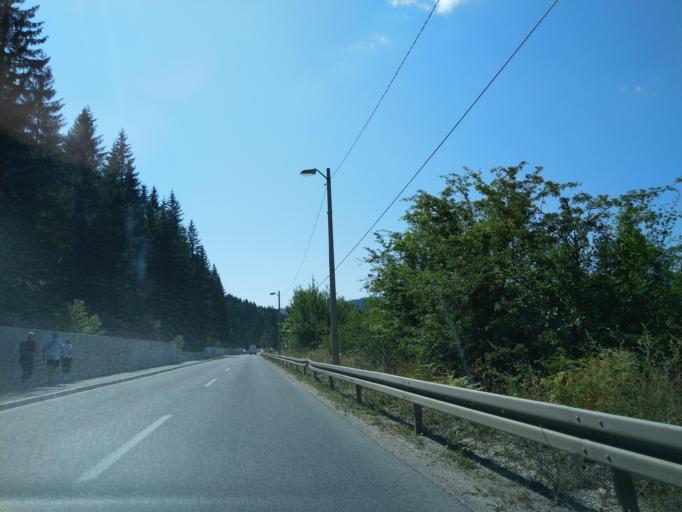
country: RS
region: Central Serbia
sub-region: Zlatiborski Okrug
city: Nova Varos
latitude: 43.4406
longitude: 19.8210
